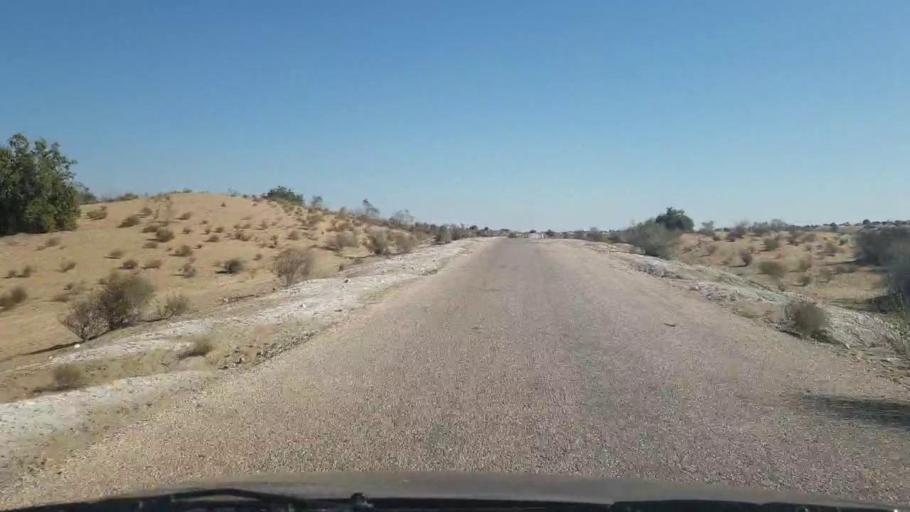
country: PK
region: Sindh
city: Bozdar
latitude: 27.0049
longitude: 68.8773
